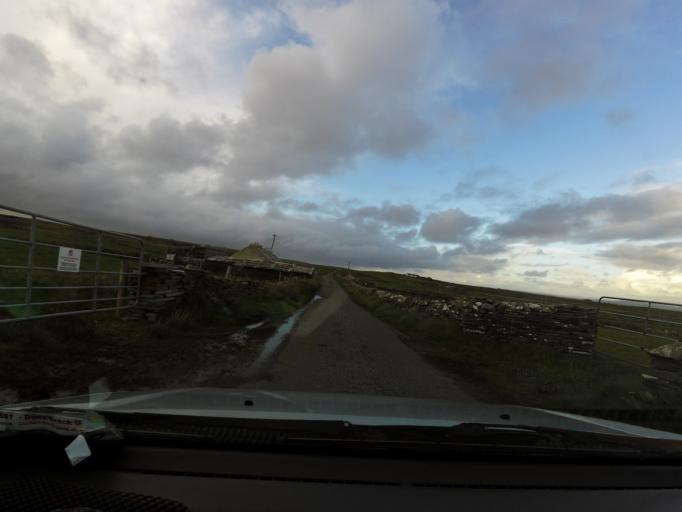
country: IE
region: Munster
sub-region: An Clar
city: Kilrush
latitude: 52.9514
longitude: -9.4419
